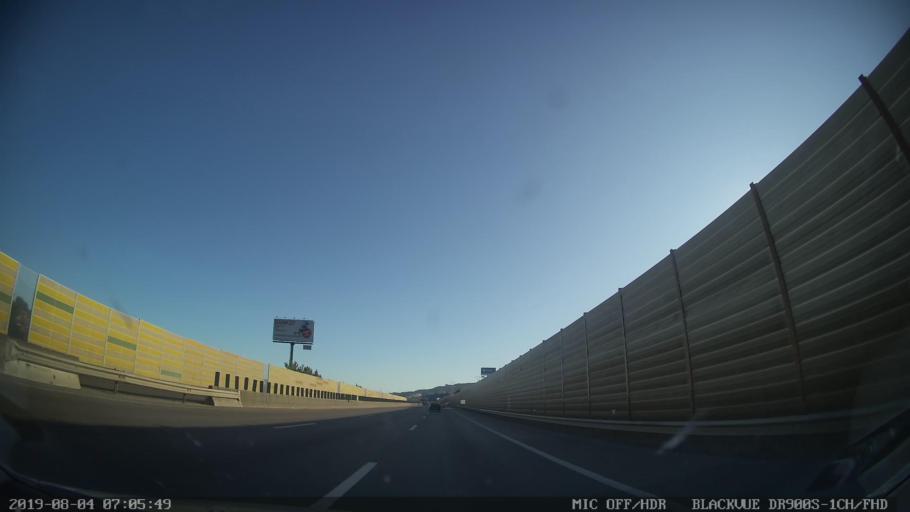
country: PT
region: Lisbon
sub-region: Vila Franca de Xira
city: Sobralinho
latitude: 38.9069
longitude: -9.0380
